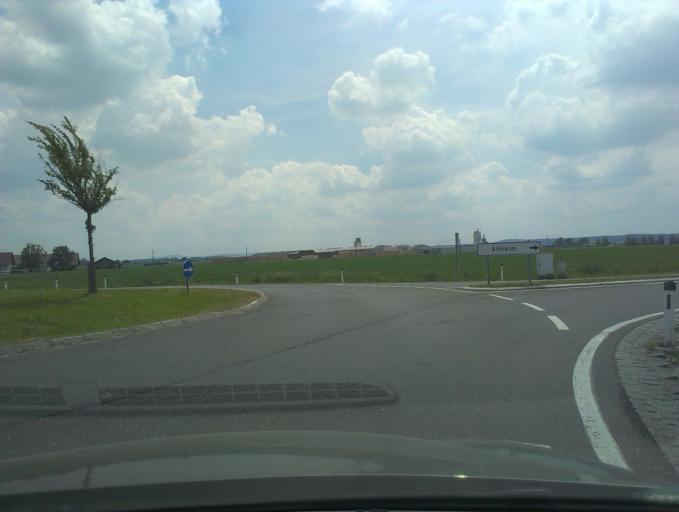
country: AT
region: Upper Austria
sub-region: Politischer Bezirk Braunau am Inn
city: Altheim
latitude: 48.2589
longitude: 13.2449
